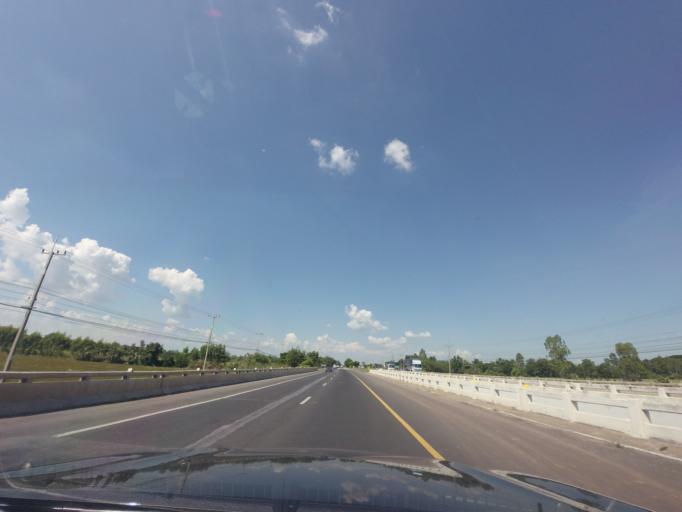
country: TH
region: Nakhon Ratchasima
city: Non Sung
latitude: 15.1993
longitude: 102.3513
